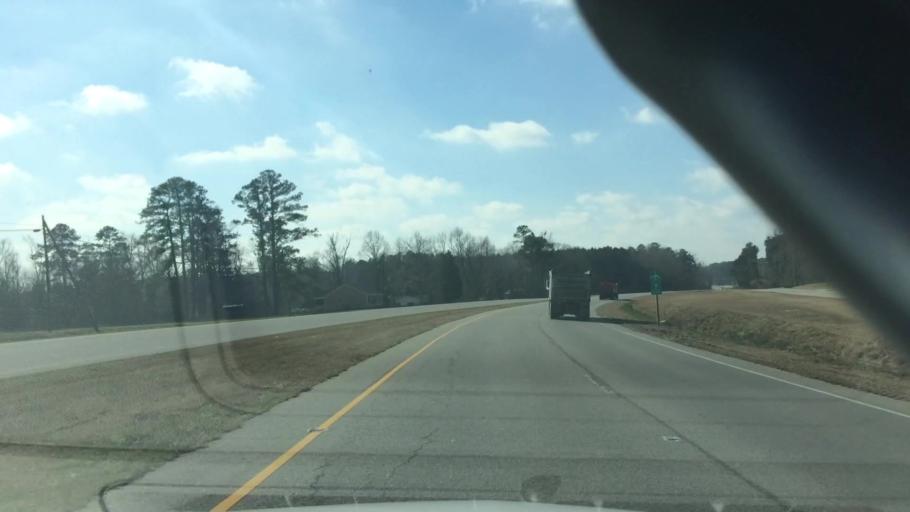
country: US
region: North Carolina
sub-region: Lenoir County
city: Kinston
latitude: 35.3131
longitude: -77.5180
